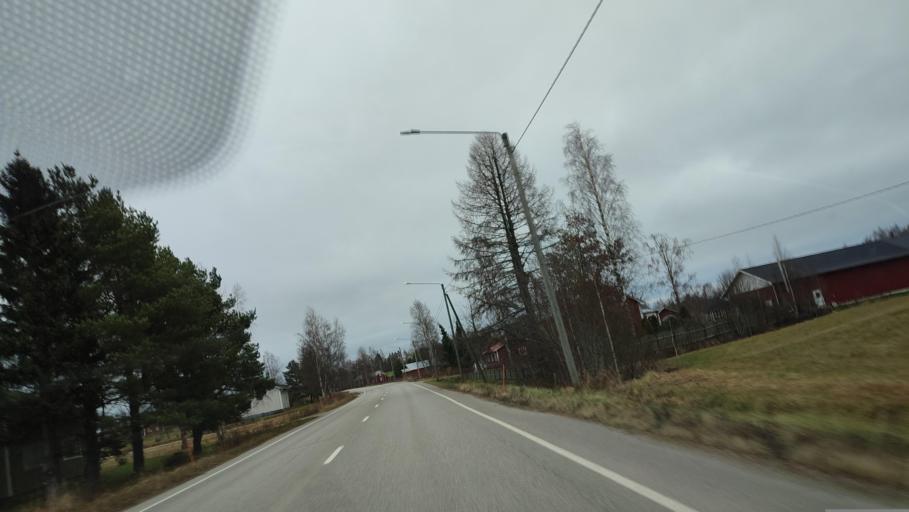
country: FI
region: Southern Ostrobothnia
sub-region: Suupohja
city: Karijoki
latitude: 62.2326
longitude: 21.6220
